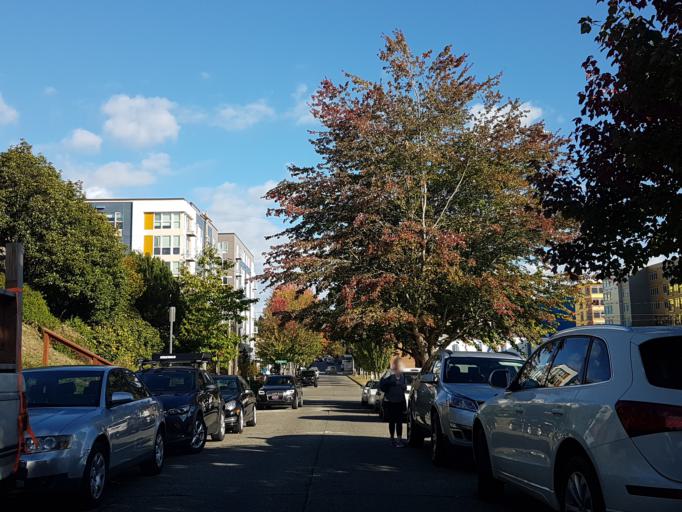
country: US
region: Washington
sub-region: King County
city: White Center
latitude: 47.5587
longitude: -122.3828
